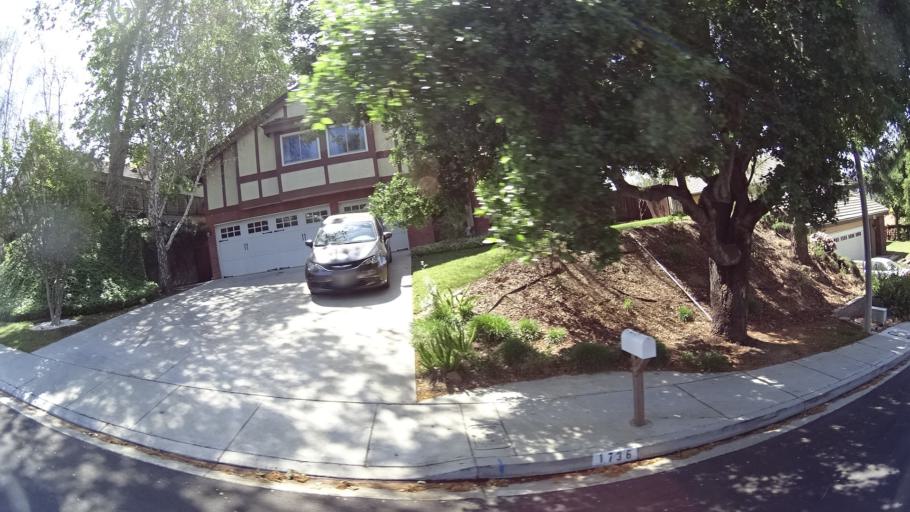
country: US
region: California
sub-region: Ventura County
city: Thousand Oaks
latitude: 34.1967
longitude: -118.8464
